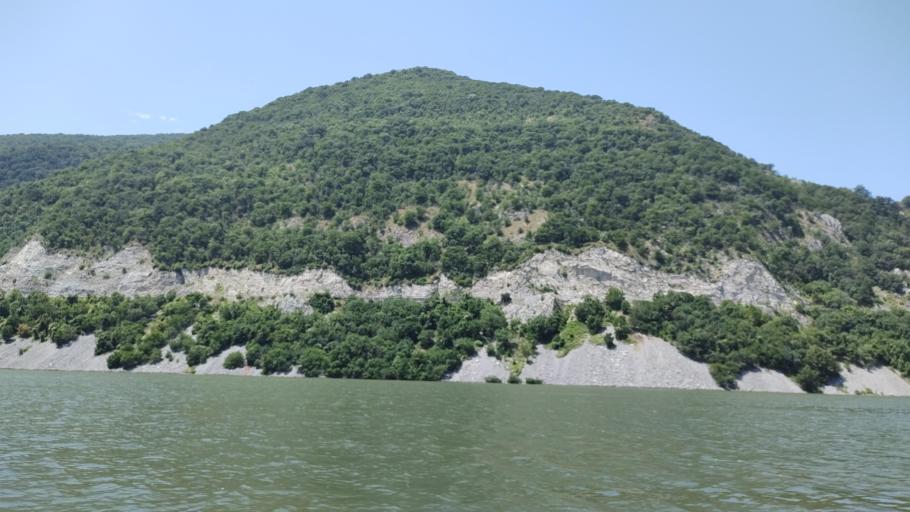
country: RO
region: Caras-Severin
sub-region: Comuna Berzasca
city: Berzasca
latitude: 44.5871
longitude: 22.0263
